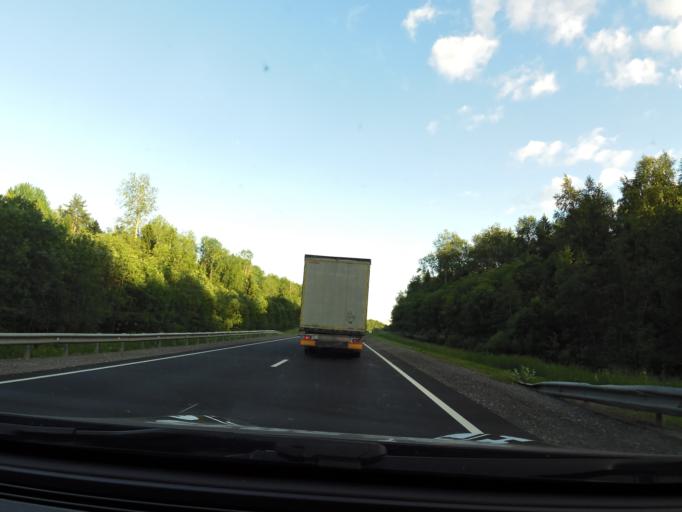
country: RU
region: Vologda
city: Gryazovets
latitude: 58.9470
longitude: 40.1725
